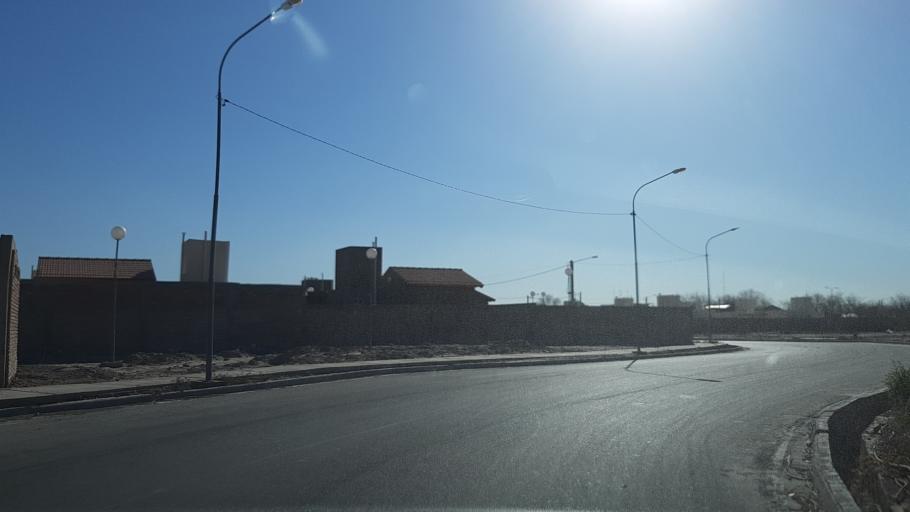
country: AR
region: San Juan
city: San Juan
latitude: -31.5197
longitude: -68.5916
